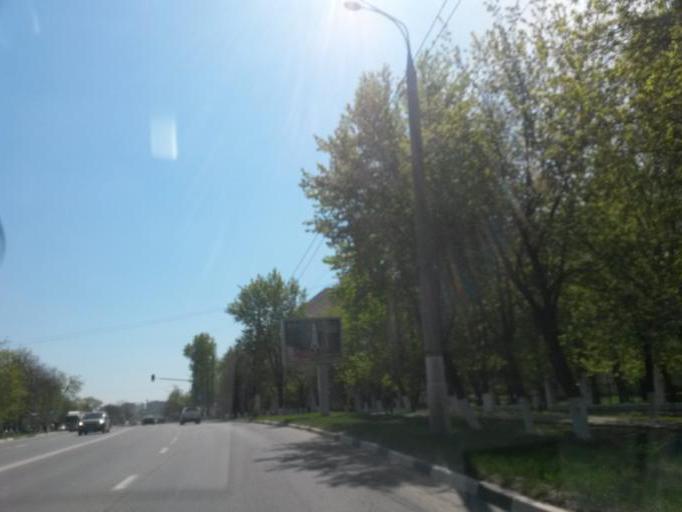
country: RU
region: Moskovskaya
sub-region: Podol'skiy Rayon
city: Podol'sk
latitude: 55.4166
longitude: 37.5473
